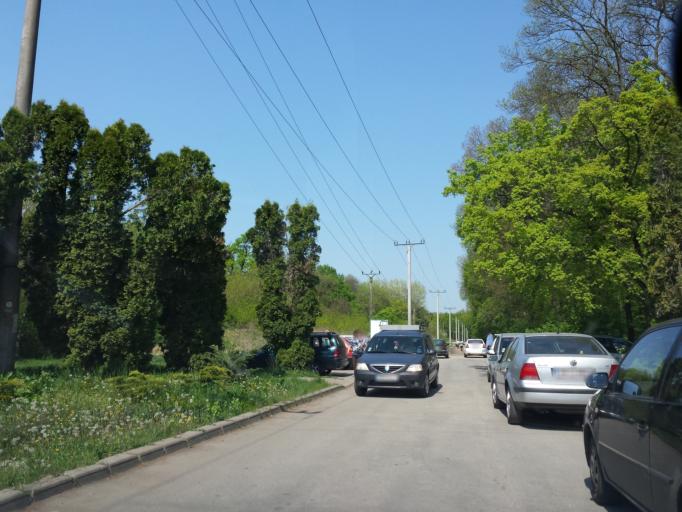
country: RO
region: Timis
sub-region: Comuna Dumbravita
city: Dumbravita
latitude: 45.7797
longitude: 21.2663
